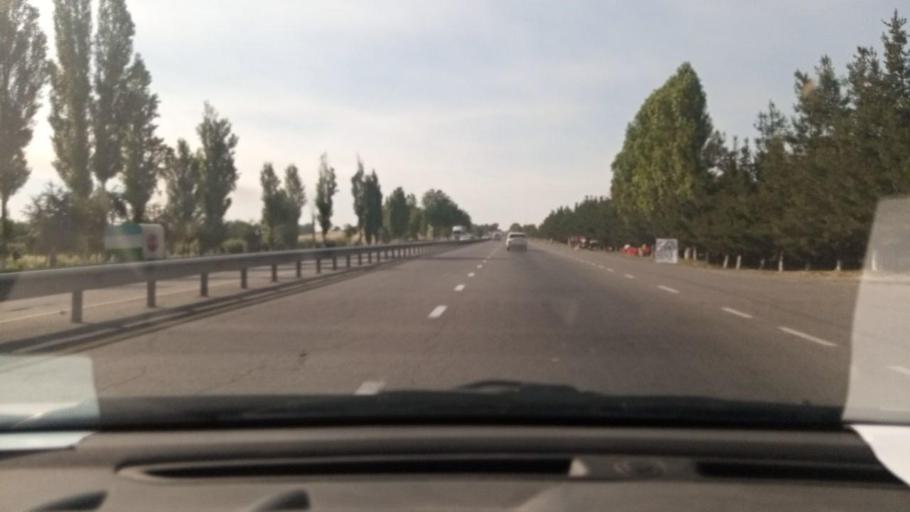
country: UZ
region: Toshkent
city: Tuytepa
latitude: 41.1177
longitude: 69.4437
